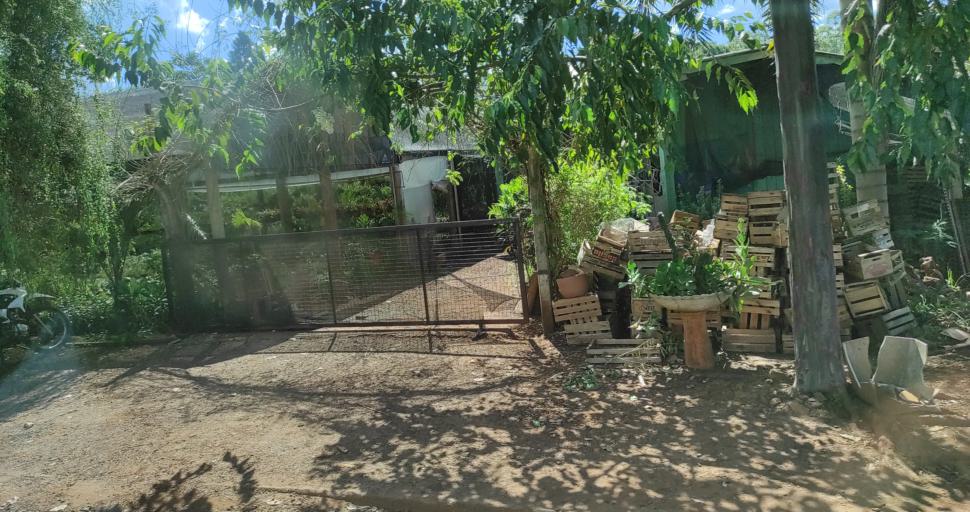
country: AR
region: Misiones
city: El Soberbio
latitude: -27.2842
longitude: -54.1977
